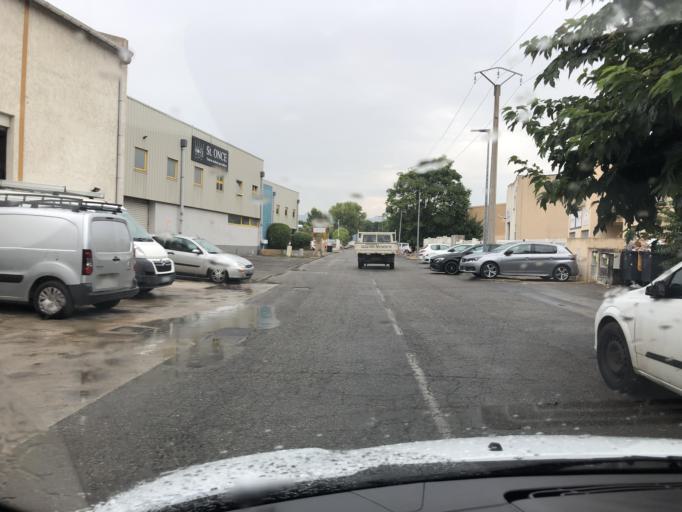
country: FR
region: Provence-Alpes-Cote d'Azur
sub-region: Departement des Bouches-du-Rhone
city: La Penne-sur-Huveaune
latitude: 43.2829
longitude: 5.5282
